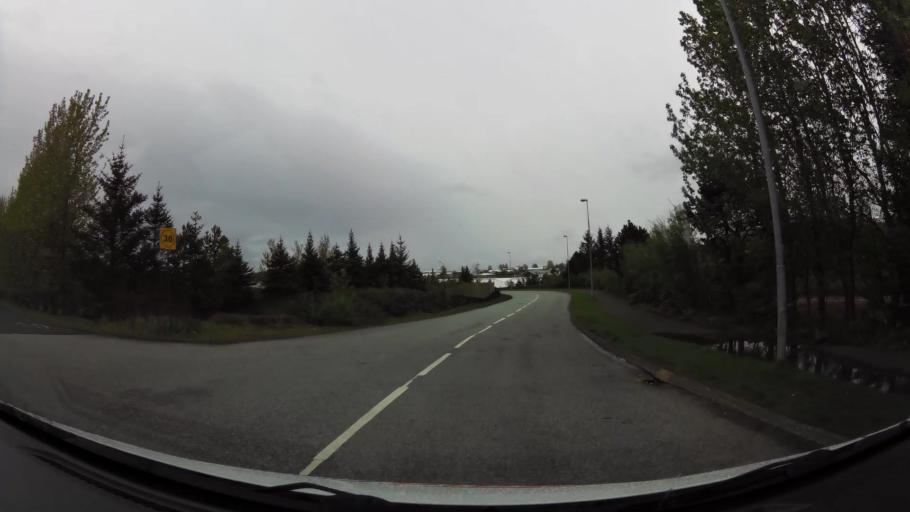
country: IS
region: Capital Region
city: Hafnarfjoerdur
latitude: 64.0638
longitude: -21.9350
